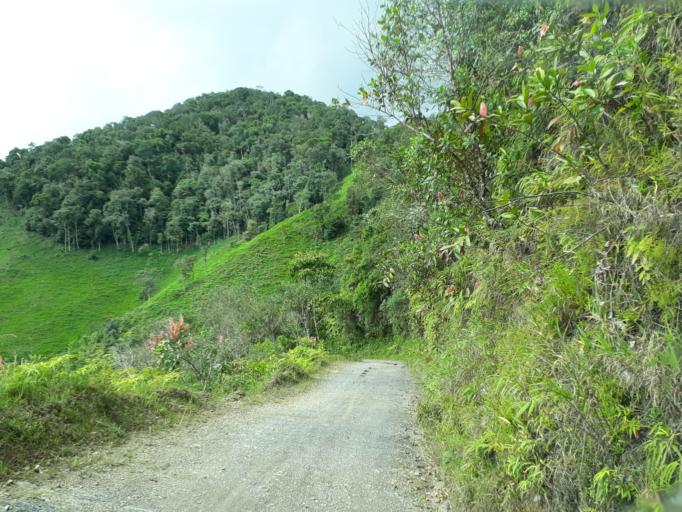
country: CO
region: Boyaca
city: Quipama
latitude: 5.3911
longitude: -74.1198
